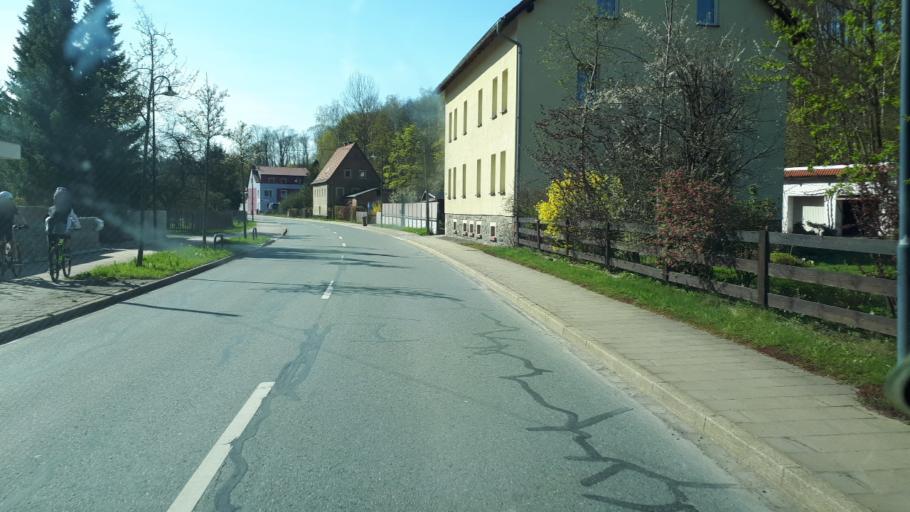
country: DE
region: Saxony
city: Chemnitz
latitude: 50.7853
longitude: 12.9611
